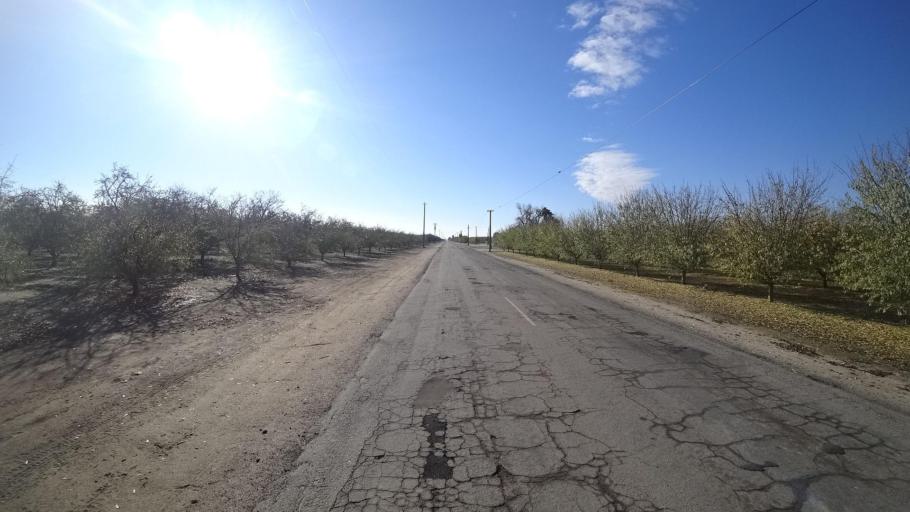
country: US
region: California
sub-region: Kern County
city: Delano
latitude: 35.7304
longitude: -119.3119
